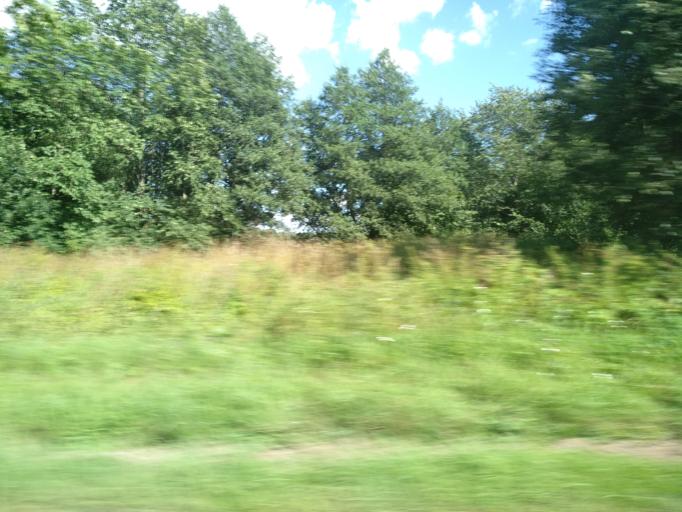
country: BY
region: Vitebsk
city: Mosar
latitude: 55.1158
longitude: 27.2068
